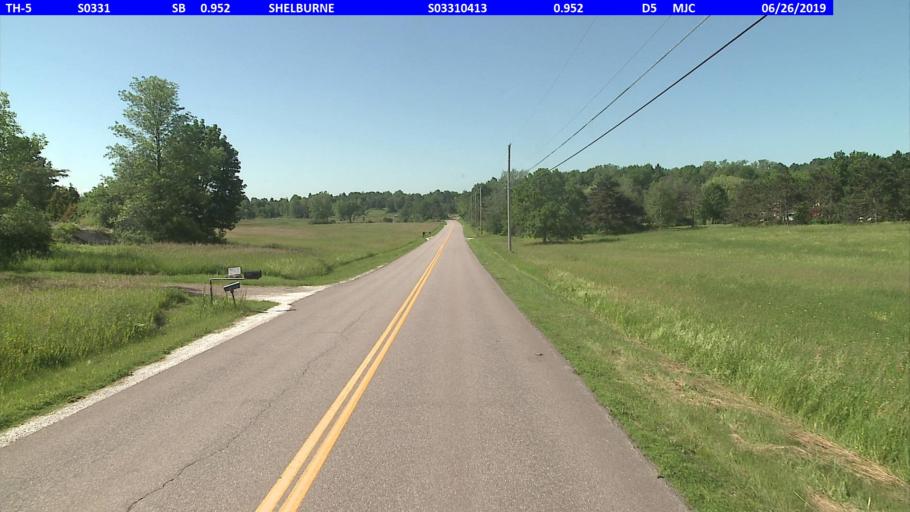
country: US
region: Vermont
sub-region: Chittenden County
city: South Burlington
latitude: 44.3846
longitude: -73.1766
